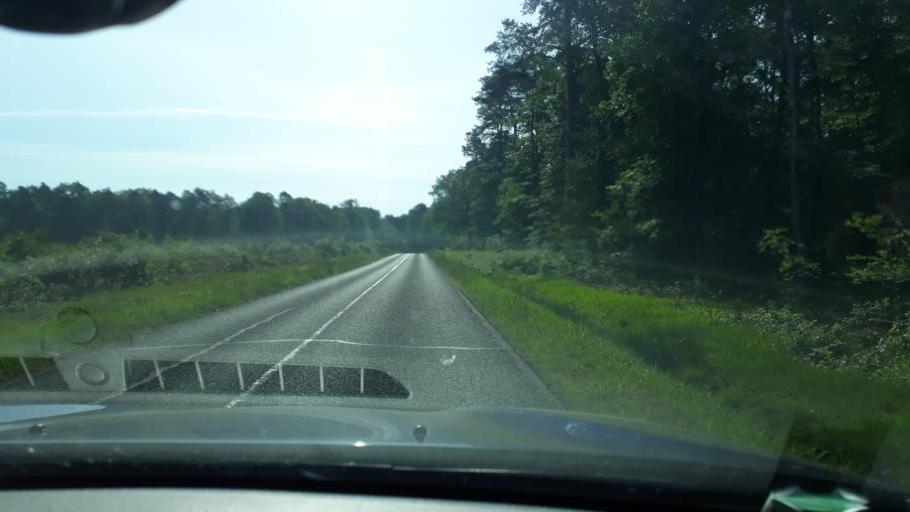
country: FR
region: Centre
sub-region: Departement du Loiret
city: Dadonville
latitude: 48.0597
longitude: 2.2478
